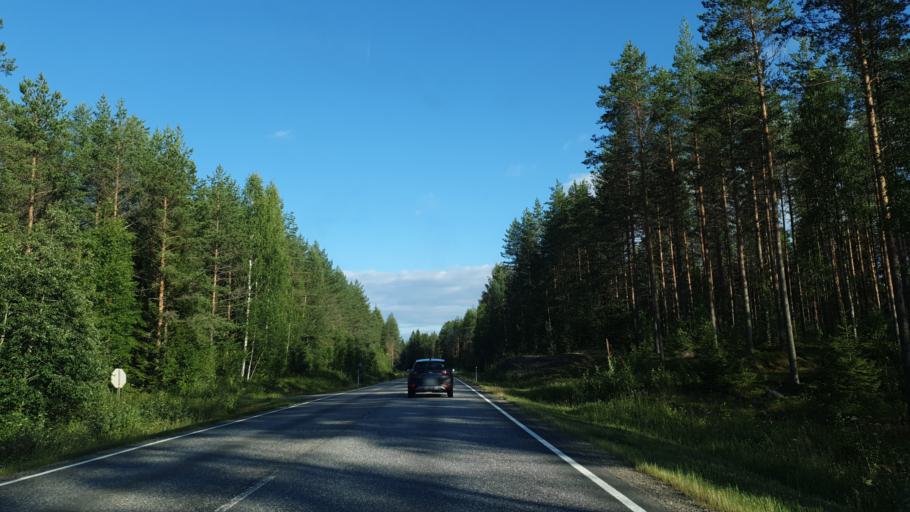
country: FI
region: North Karelia
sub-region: Joensuu
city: Outokumpu
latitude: 62.5241
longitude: 28.9991
